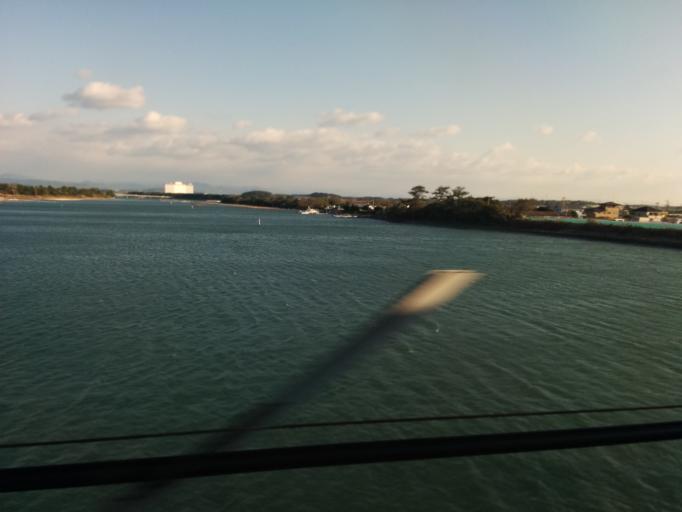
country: JP
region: Shizuoka
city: Kosai-shi
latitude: 34.6890
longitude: 137.6067
